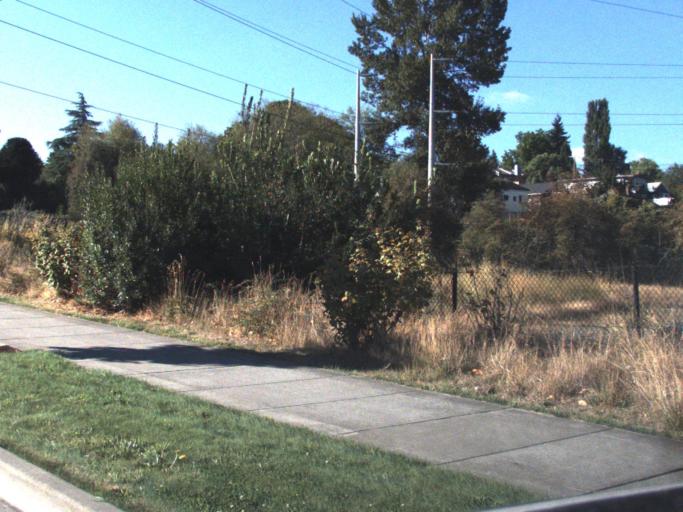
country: US
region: Washington
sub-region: King County
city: Renton
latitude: 47.4676
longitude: -122.2080
